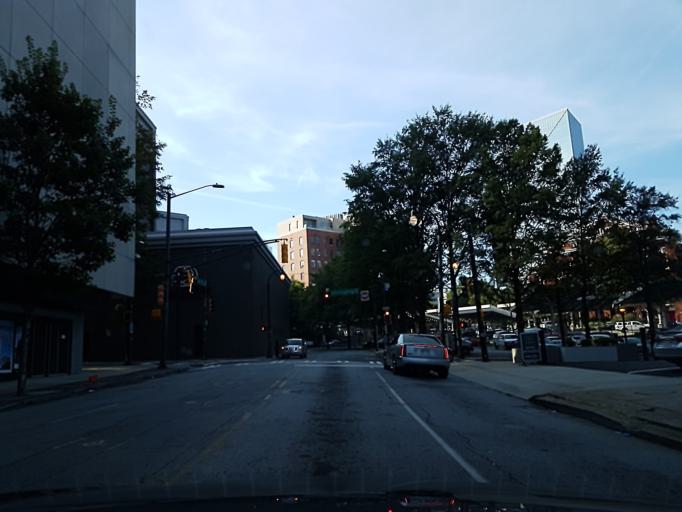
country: US
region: Georgia
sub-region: Fulton County
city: Atlanta
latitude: 33.7601
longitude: -84.3905
